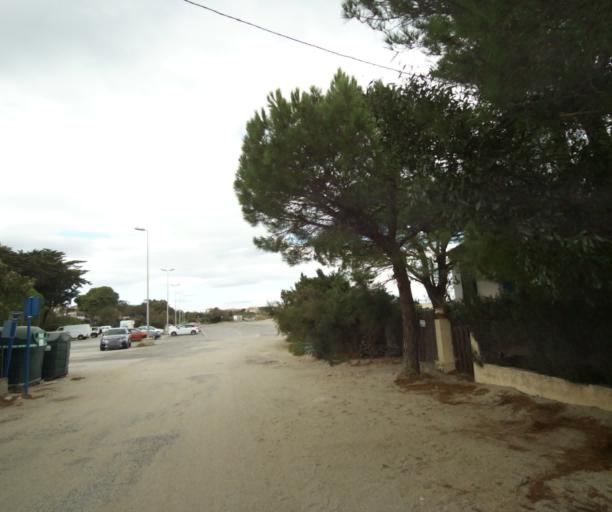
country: FR
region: Languedoc-Roussillon
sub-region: Departement des Pyrenees-Orientales
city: Collioure
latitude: 42.5374
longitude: 3.0555
